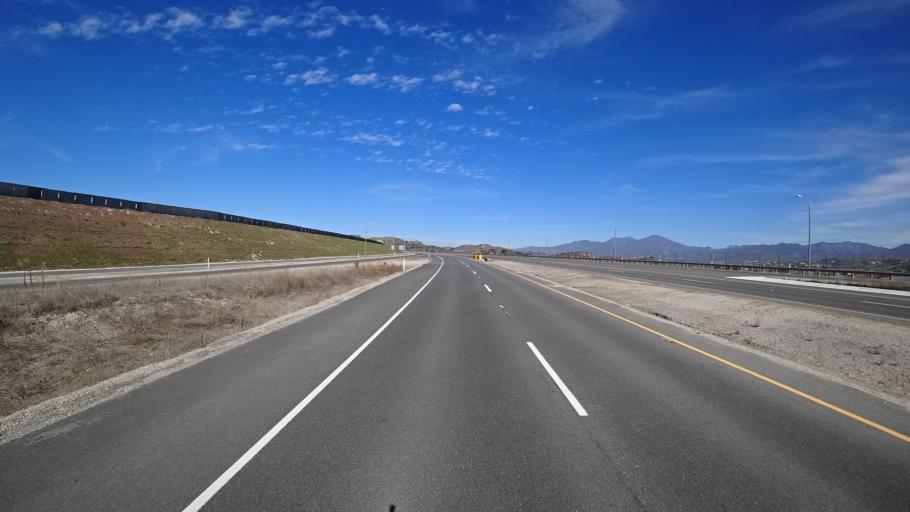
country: US
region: California
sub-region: Orange County
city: Ladera Ranch
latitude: 33.5493
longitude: -117.5941
